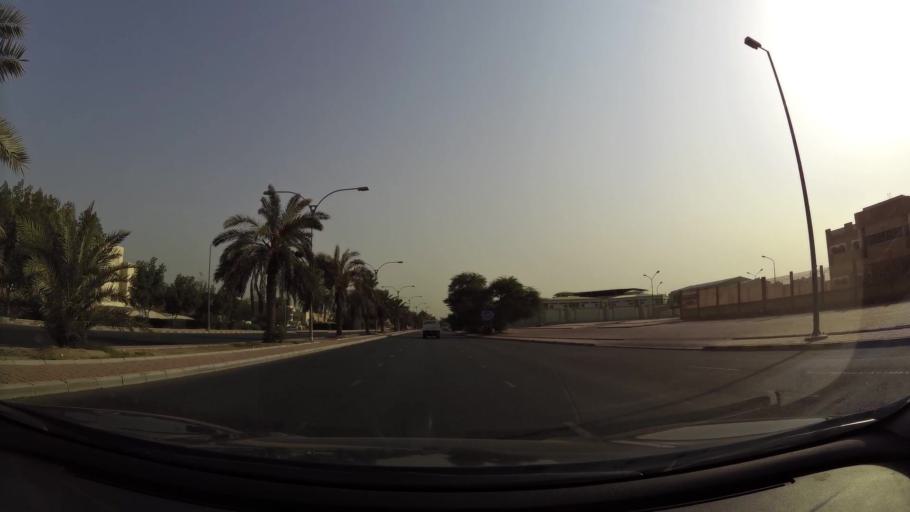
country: KW
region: Al Ahmadi
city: Ar Riqqah
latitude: 29.1298
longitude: 48.1037
